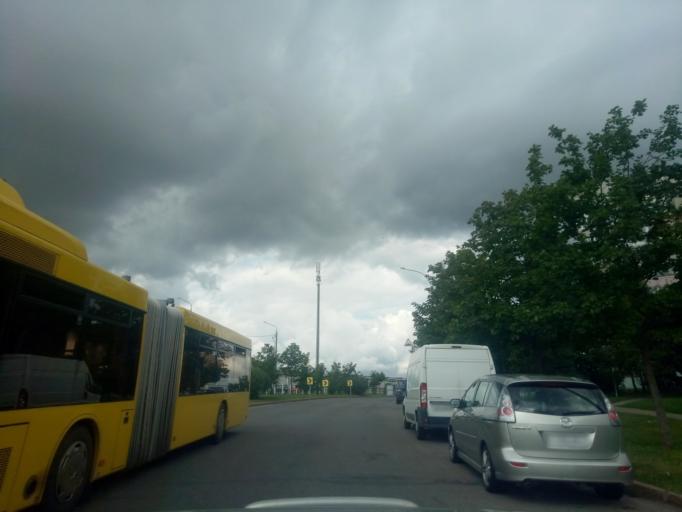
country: BY
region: Minsk
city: Malinovka
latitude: 53.8813
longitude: 27.4201
